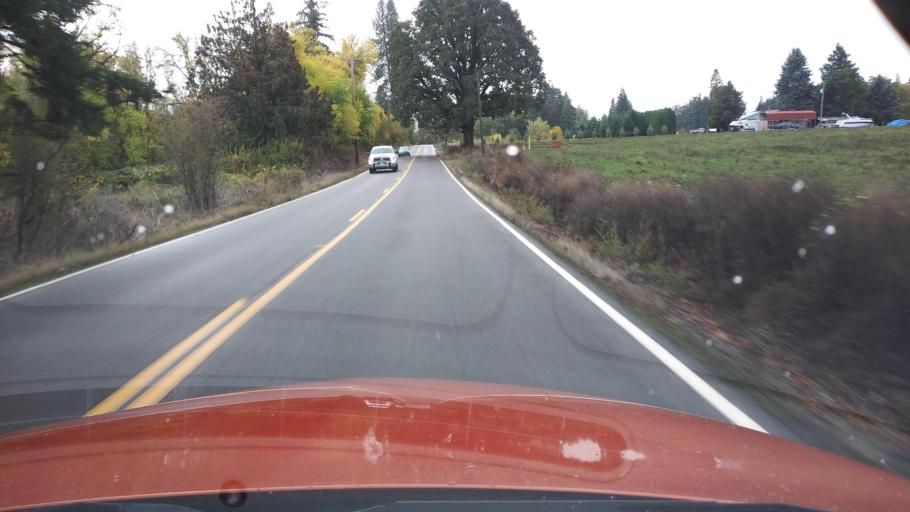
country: US
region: Oregon
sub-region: Washington County
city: Forest Grove
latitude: 45.5336
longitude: -123.0871
